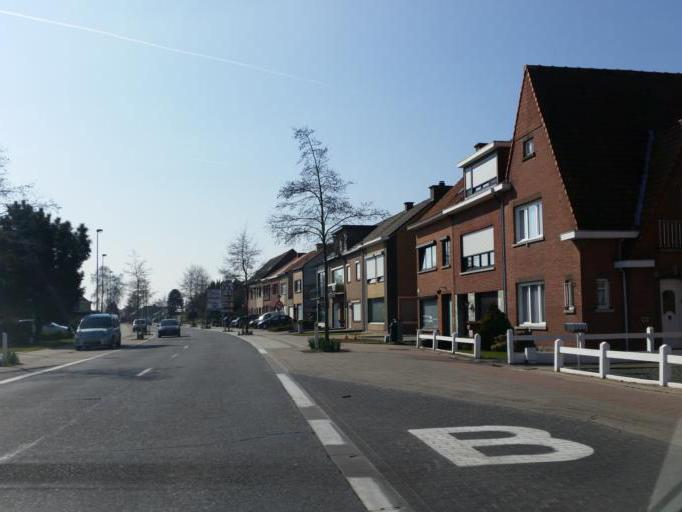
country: BE
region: Flanders
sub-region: Provincie Oost-Vlaanderen
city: Kruibeke
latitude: 51.1622
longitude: 4.3059
